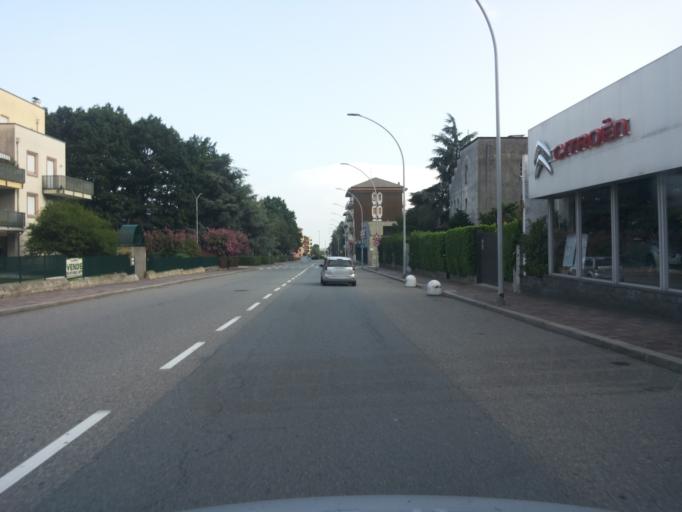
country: IT
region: Piedmont
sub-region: Provincia di Biella
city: Biella
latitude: 45.5579
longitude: 8.0534
